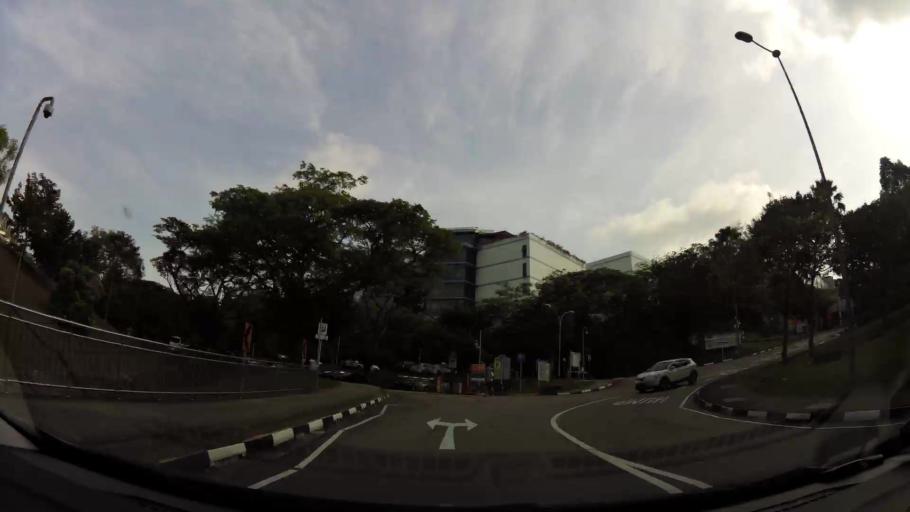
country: SG
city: Singapore
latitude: 1.2936
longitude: 103.7753
